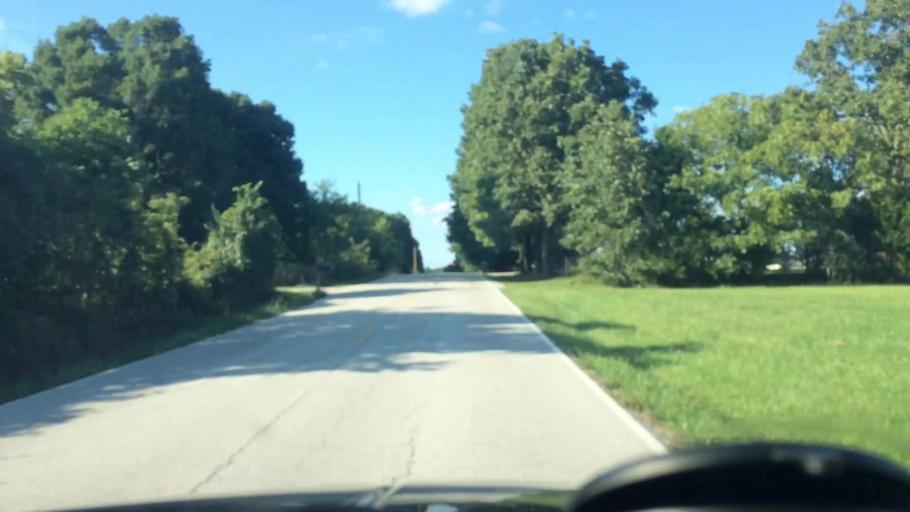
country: US
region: Missouri
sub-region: Greene County
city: Strafford
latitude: 37.2806
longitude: -93.0812
